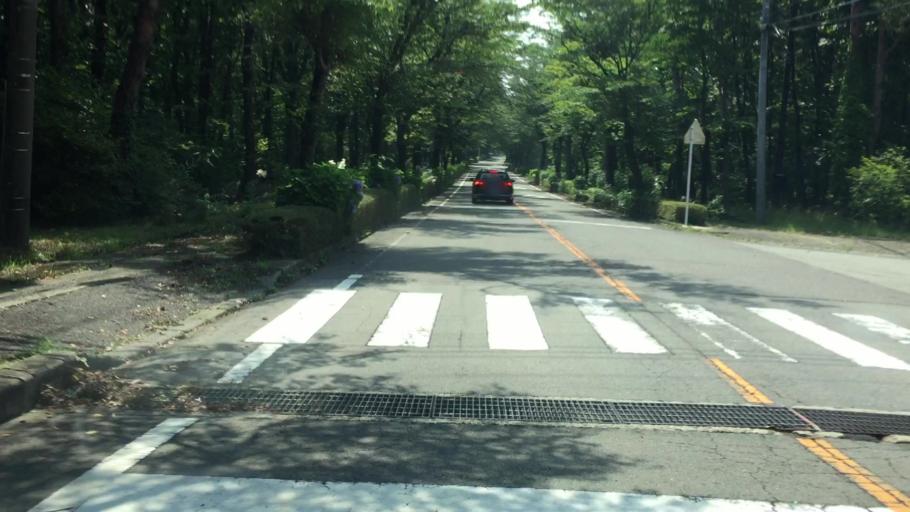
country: JP
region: Tochigi
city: Kuroiso
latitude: 37.1000
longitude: 140.0386
